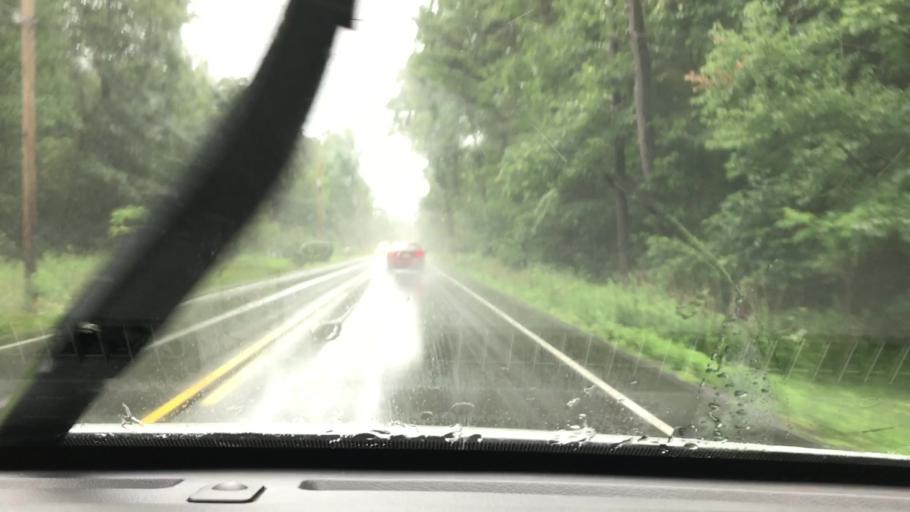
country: US
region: Pennsylvania
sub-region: Blair County
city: Tyrone
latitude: 40.7301
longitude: -78.1905
